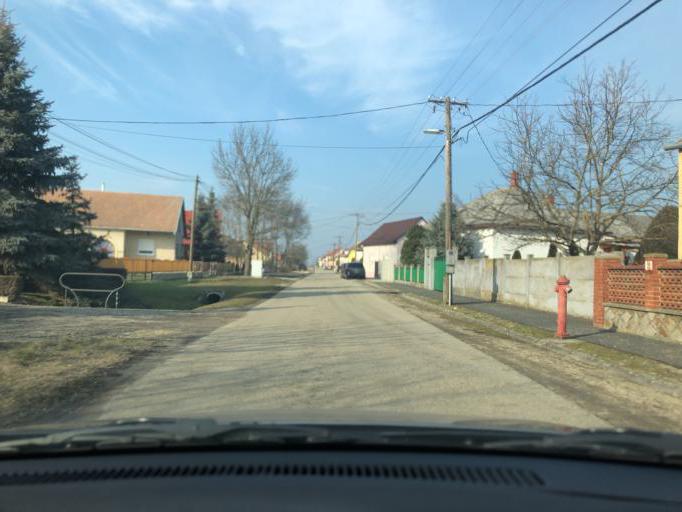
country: HU
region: Gyor-Moson-Sopron
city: Kapuvar
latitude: 47.5786
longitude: 17.0765
